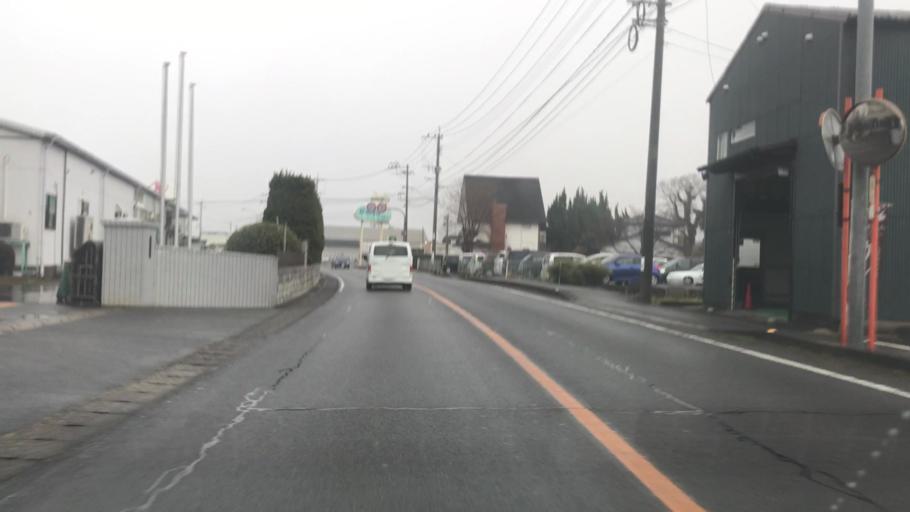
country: JP
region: Saga Prefecture
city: Takeocho-takeo
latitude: 33.2108
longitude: 130.0460
